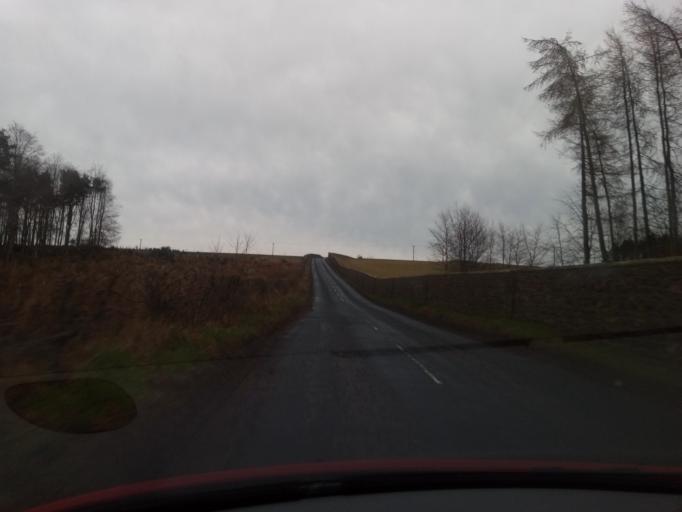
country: GB
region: England
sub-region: Northumberland
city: Alnwick
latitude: 55.4440
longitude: -1.7384
